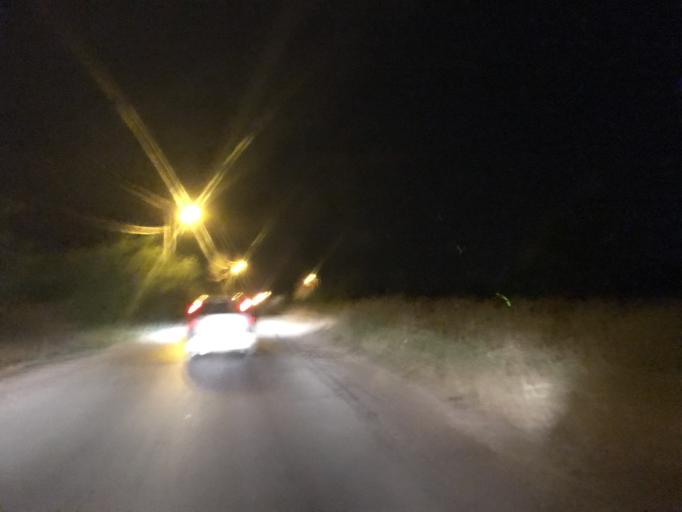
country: RS
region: Central Serbia
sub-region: Belgrade
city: Zvezdara
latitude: 44.7792
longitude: 20.5474
